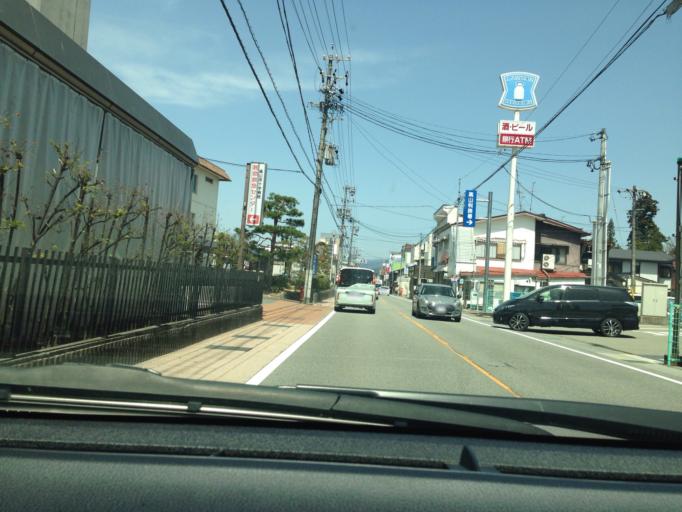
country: JP
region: Gifu
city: Takayama
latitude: 36.1365
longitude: 137.2552
